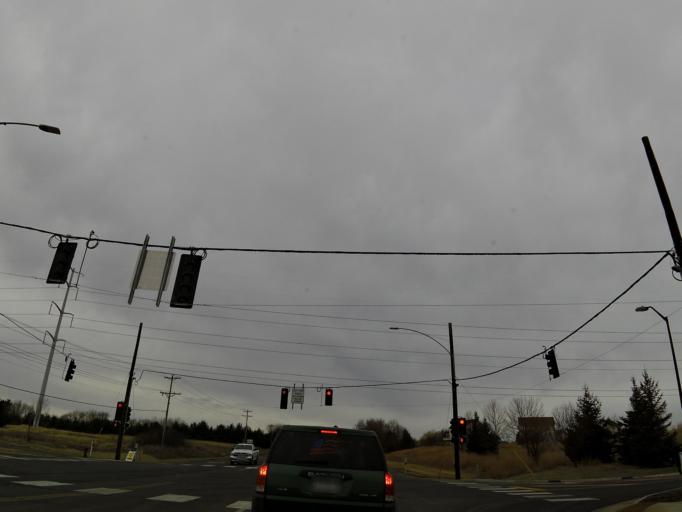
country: US
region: Minnesota
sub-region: Washington County
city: Saint Paul Park
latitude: 44.8479
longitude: -92.9675
